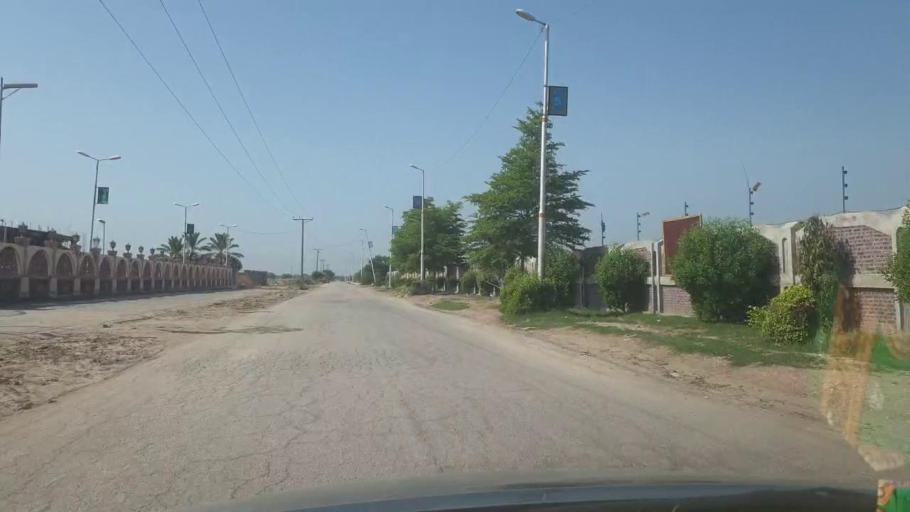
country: PK
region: Sindh
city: Rohri
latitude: 27.5219
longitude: 69.0364
